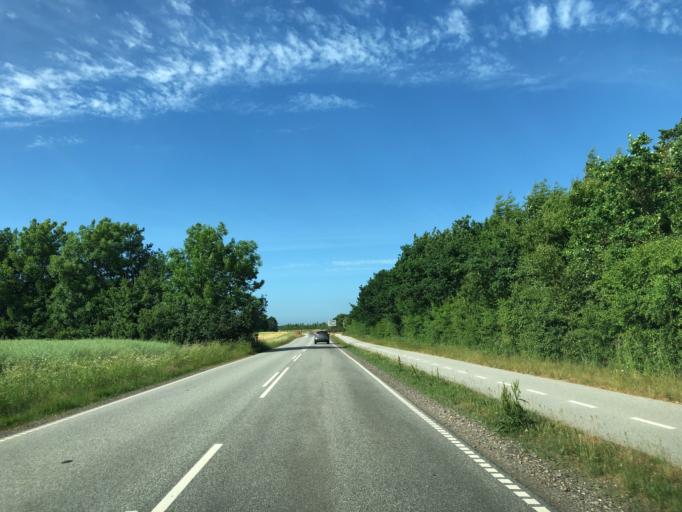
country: DK
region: Central Jutland
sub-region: Herning Kommune
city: Snejbjerg
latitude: 56.1137
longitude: 8.9079
